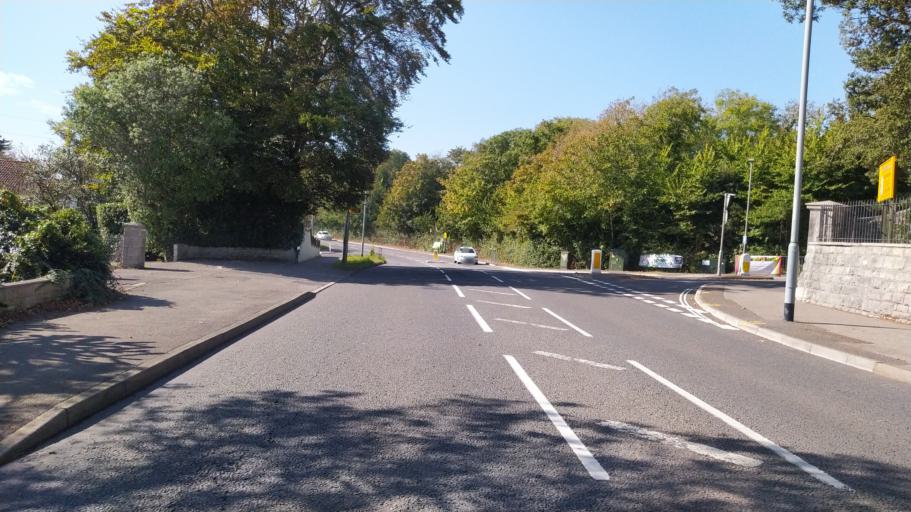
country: GB
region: England
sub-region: Dorset
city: Weymouth
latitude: 50.6002
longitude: -2.4652
